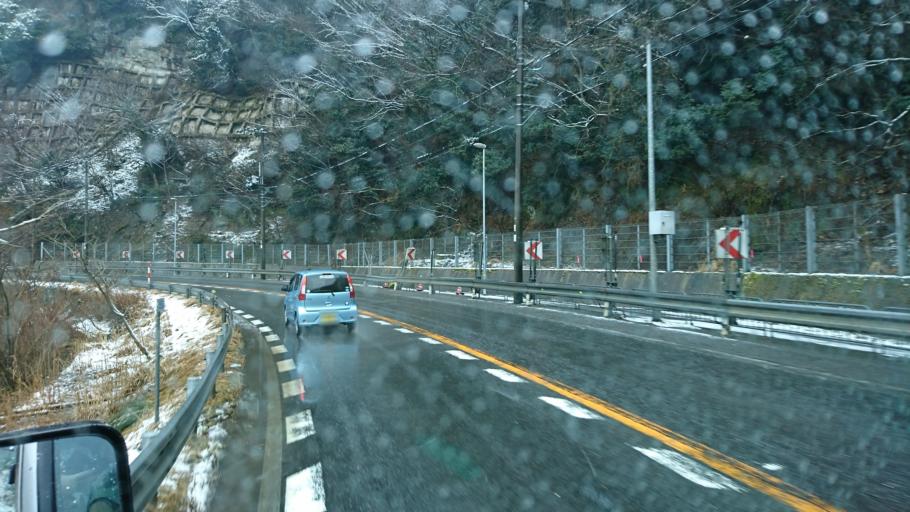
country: JP
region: Hyogo
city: Toyooka
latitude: 35.4799
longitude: 134.5863
